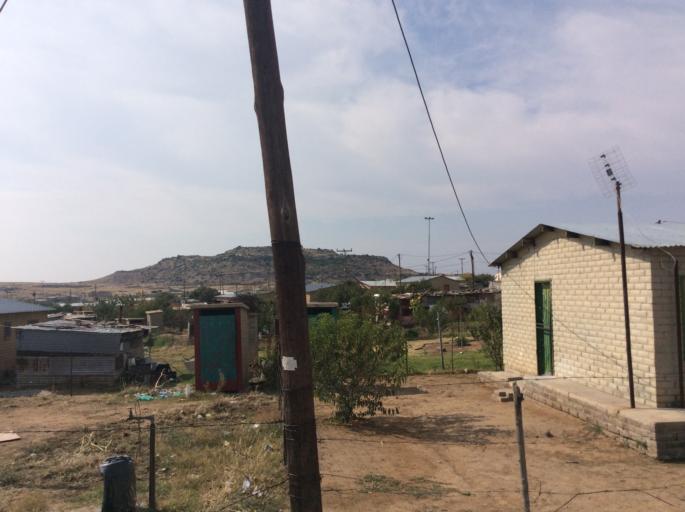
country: ZA
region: Orange Free State
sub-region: Xhariep District Municipality
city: Dewetsdorp
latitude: -29.5939
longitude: 26.6788
